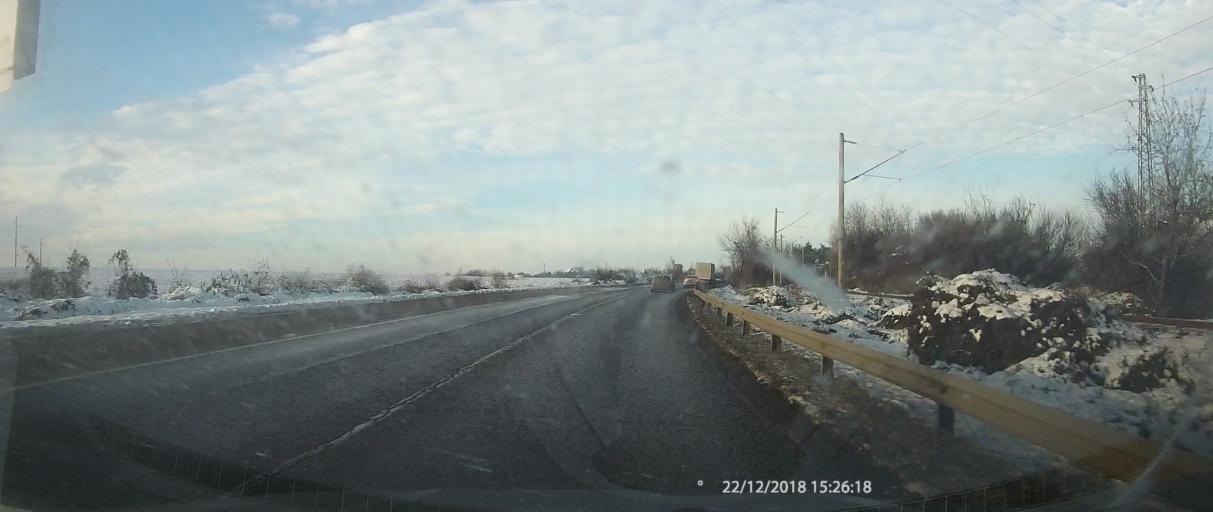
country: RO
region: Giurgiu
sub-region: Comuna Slobozia
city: Slobozia
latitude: 43.7706
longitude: 25.8979
